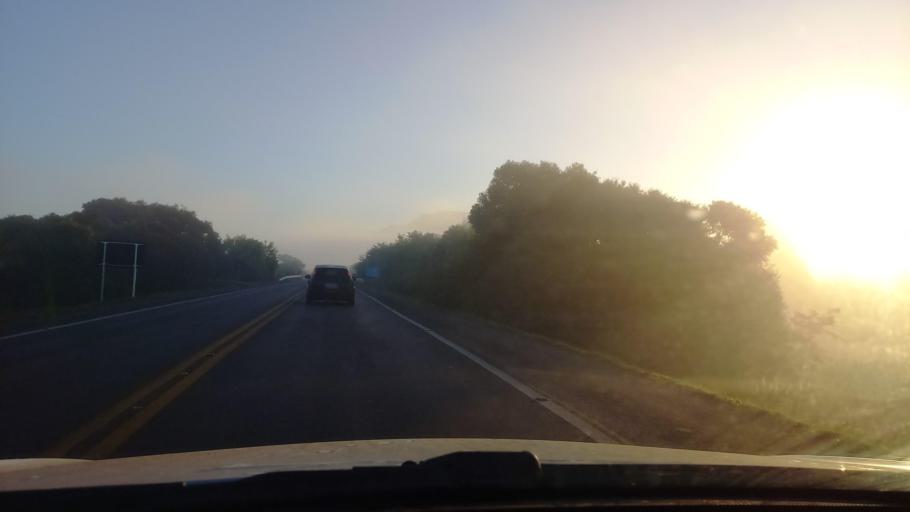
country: BR
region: Rio Grande do Sul
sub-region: Candelaria
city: Candelaria
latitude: -29.6750
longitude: -52.7708
